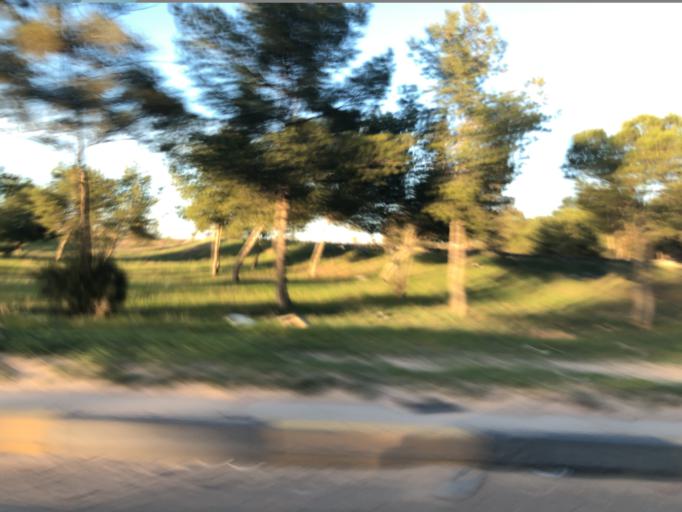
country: LY
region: Tripoli
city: Tagiura
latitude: 32.8691
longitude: 13.2878
